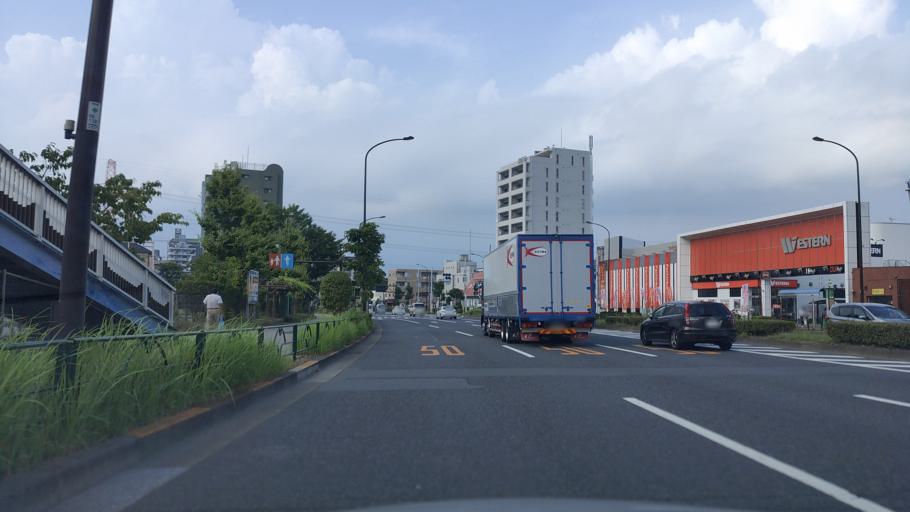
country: JP
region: Tokyo
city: Urayasu
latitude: 35.6477
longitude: 139.8714
